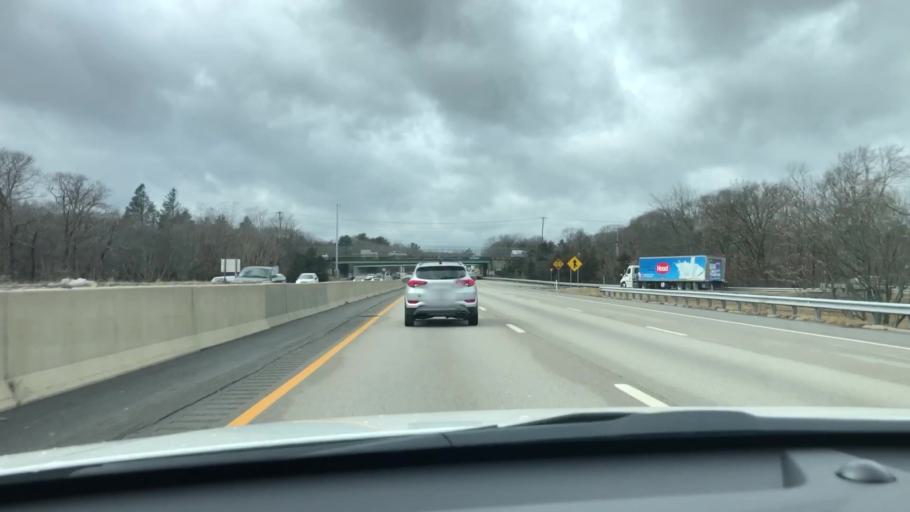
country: US
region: Massachusetts
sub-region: Norfolk County
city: Weymouth
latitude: 42.1939
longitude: -70.9531
